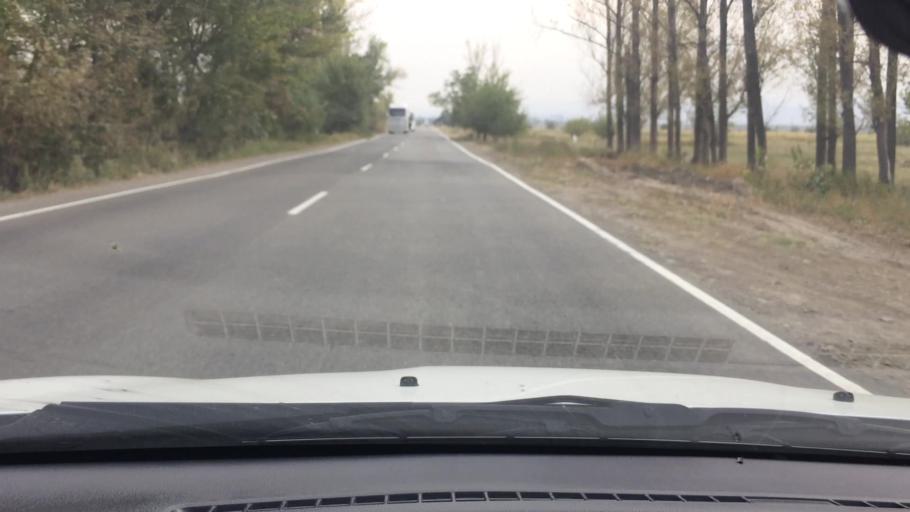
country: GE
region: Kvemo Kartli
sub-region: Gardabani
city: Gardabani
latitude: 41.4455
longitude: 44.9972
